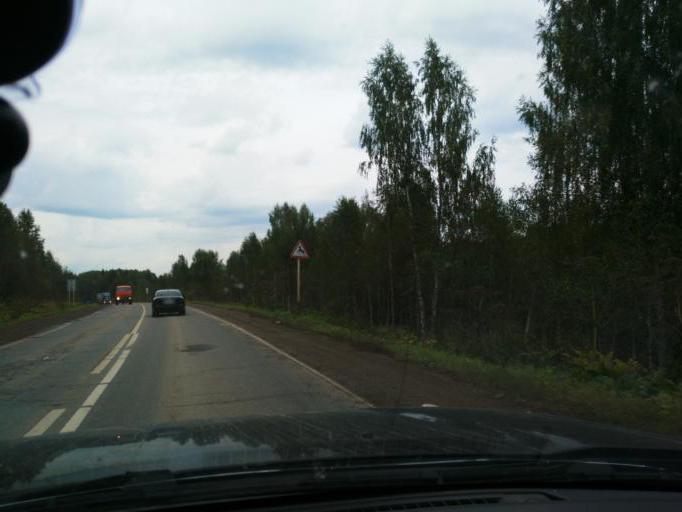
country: RU
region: Perm
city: Chernushka
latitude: 56.6825
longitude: 56.1781
